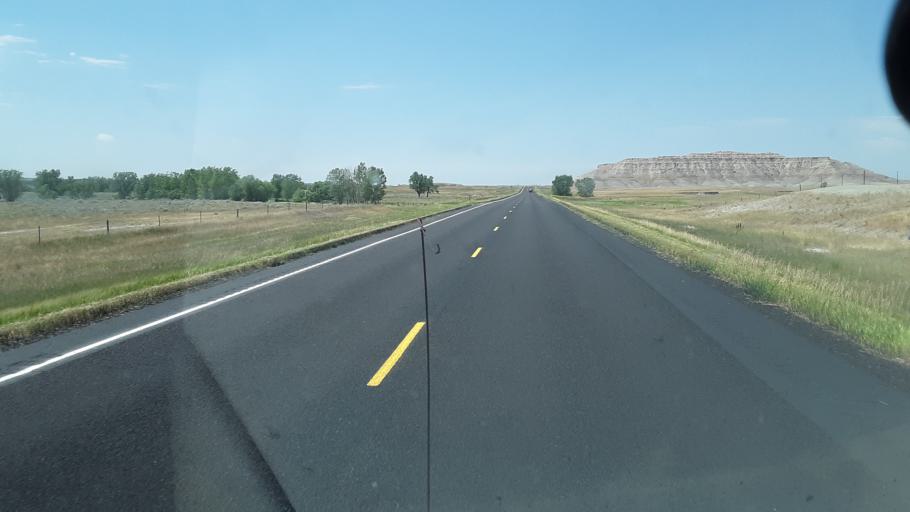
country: US
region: South Dakota
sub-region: Haakon County
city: Philip
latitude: 43.7193
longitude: -102.0094
